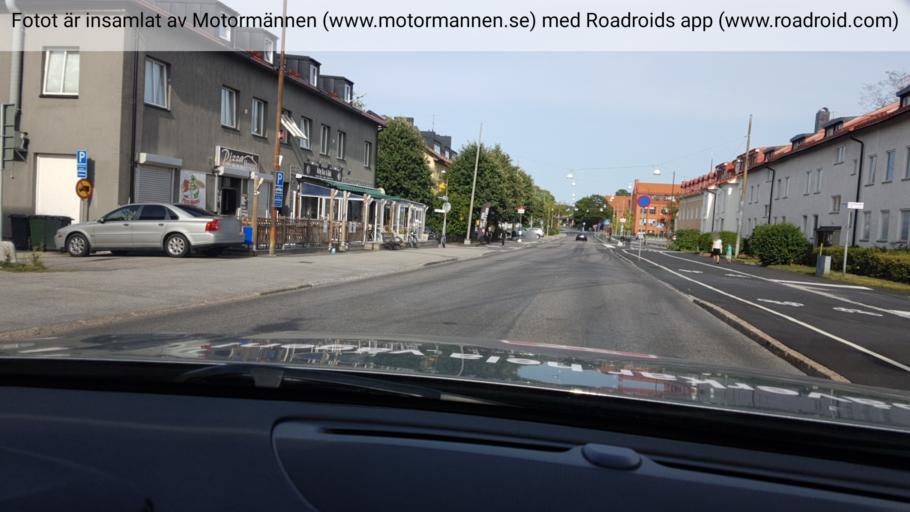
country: SE
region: Stockholm
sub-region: Stockholms Kommun
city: Arsta
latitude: 59.2730
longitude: 18.0219
